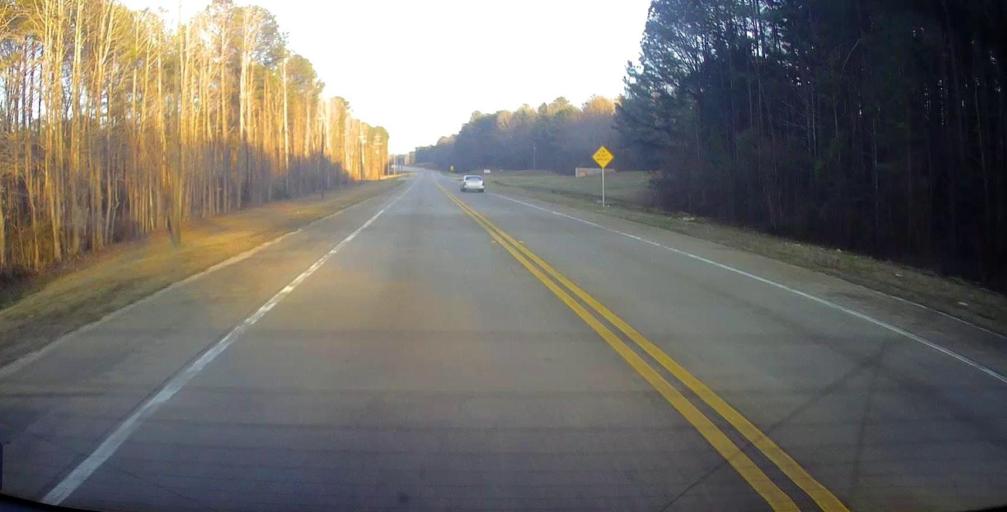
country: US
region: Georgia
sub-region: Troup County
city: La Grange
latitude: 32.9893
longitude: -85.0542
